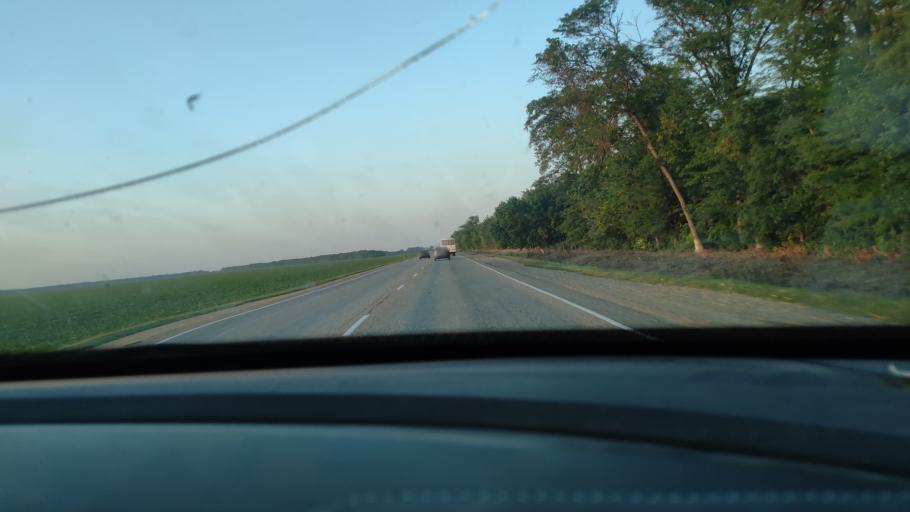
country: RU
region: Krasnodarskiy
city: Starominskaya
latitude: 46.4514
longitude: 39.0304
